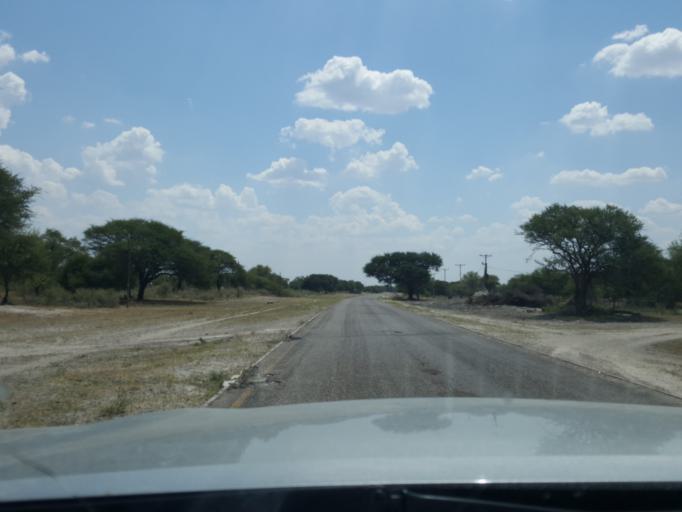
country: BW
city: Tsau
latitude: -20.1790
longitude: 22.4627
